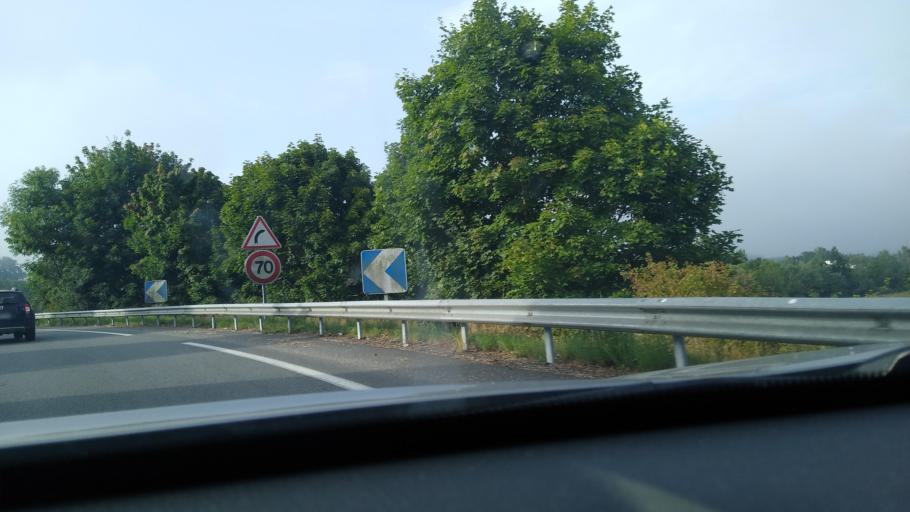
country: FR
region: Midi-Pyrenees
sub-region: Departement de la Haute-Garonne
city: Salies-du-Salat
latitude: 43.1293
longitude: 0.9417
